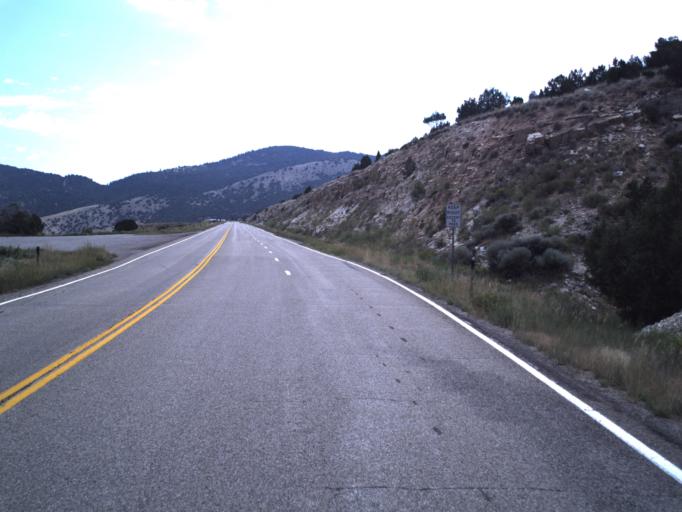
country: US
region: Utah
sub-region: Daggett County
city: Manila
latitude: 40.9163
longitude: -109.6892
